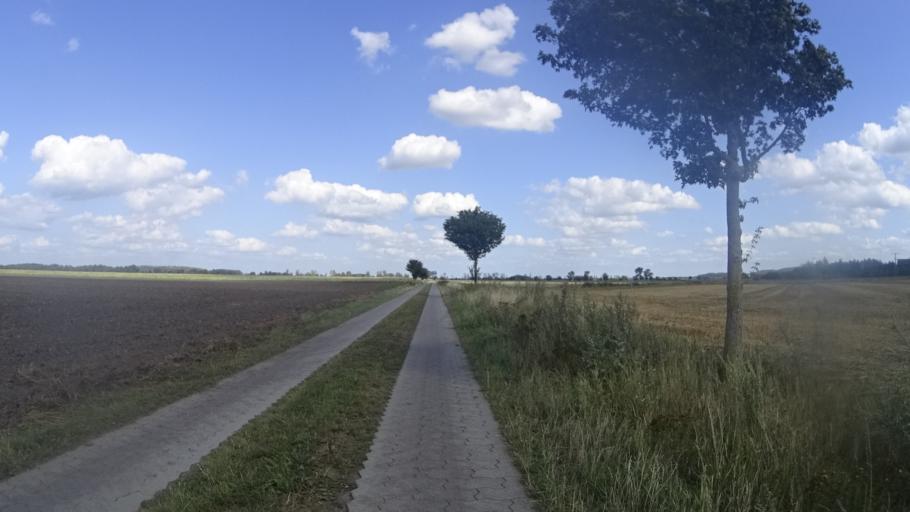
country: DE
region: Brandenburg
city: Rhinow
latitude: 52.7616
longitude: 12.2996
